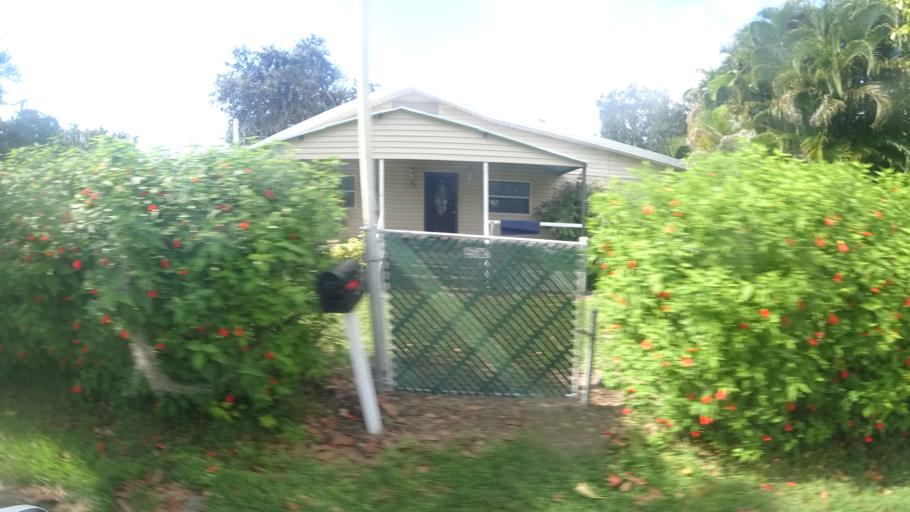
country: US
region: Florida
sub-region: Manatee County
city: Memphis
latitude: 27.5822
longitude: -82.5594
